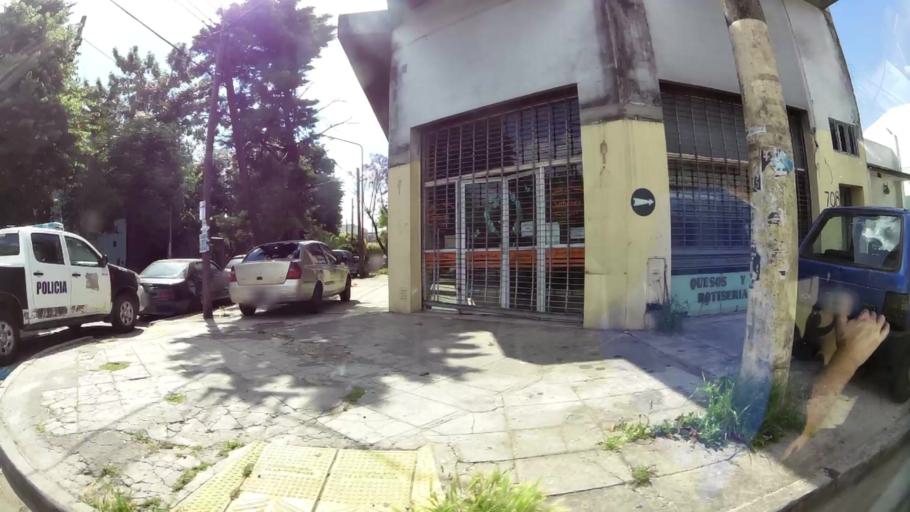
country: AR
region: Buenos Aires
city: San Justo
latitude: -34.6471
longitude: -58.5454
